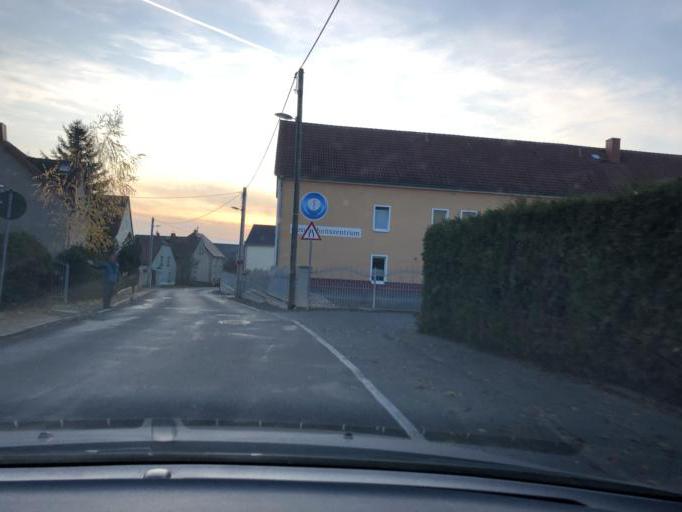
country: DE
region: Saxony
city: Nerchau
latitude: 51.2622
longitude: 12.7931
